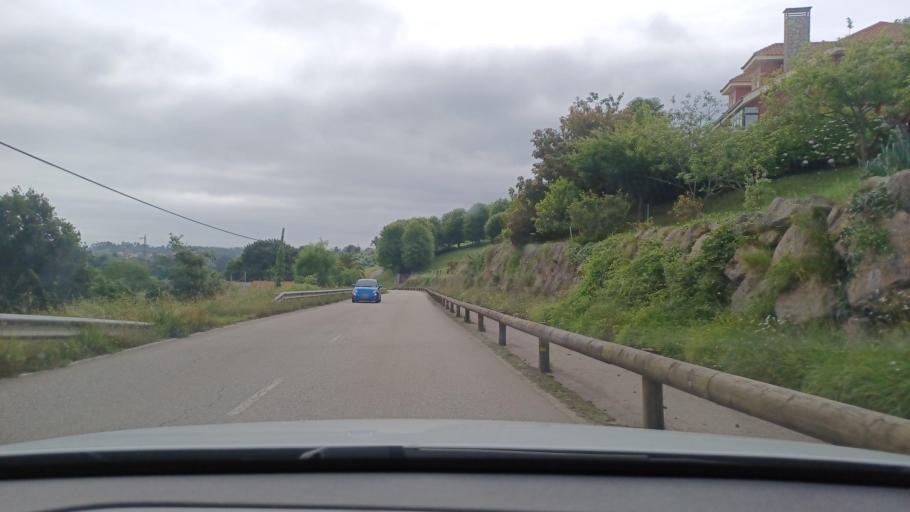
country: ES
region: Asturias
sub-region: Province of Asturias
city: Ribadesella
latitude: 43.4551
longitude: -5.1014
